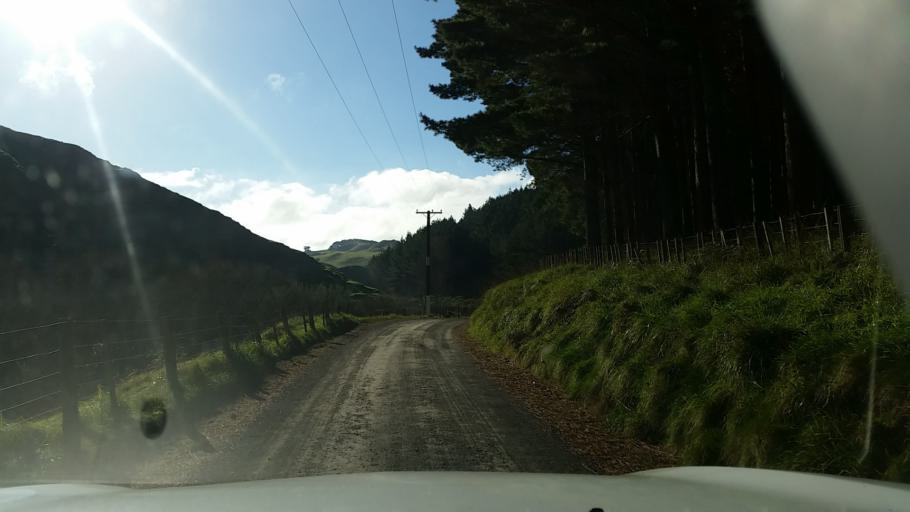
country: NZ
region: Taranaki
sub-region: South Taranaki District
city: Eltham
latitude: -39.5049
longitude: 174.4008
